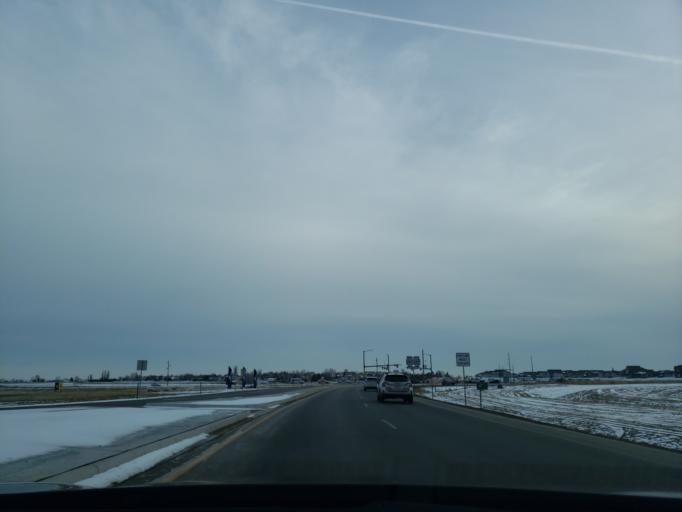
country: US
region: Colorado
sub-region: Larimer County
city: Campion
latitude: 40.3378
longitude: -105.0936
